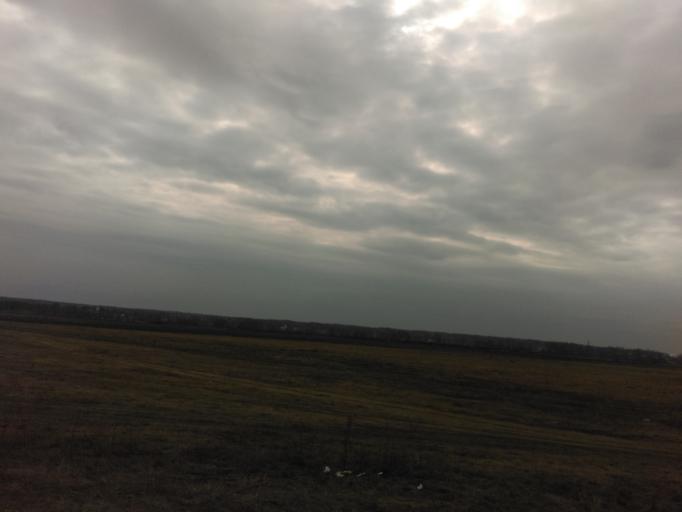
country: RU
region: Moskovskaya
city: Nikolina Gora
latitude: 55.7377
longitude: 37.0125
